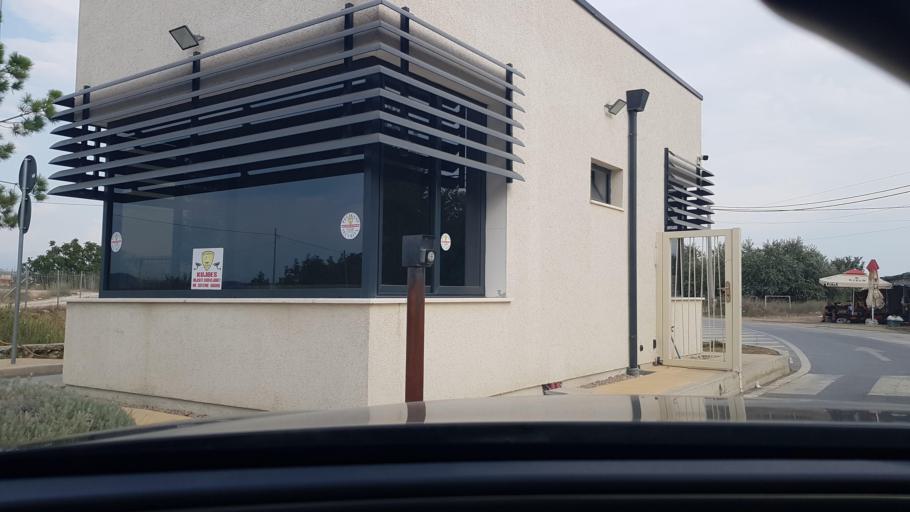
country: AL
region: Durres
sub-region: Rrethi i Durresit
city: Katundi i Ri
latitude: 41.4873
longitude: 19.5126
